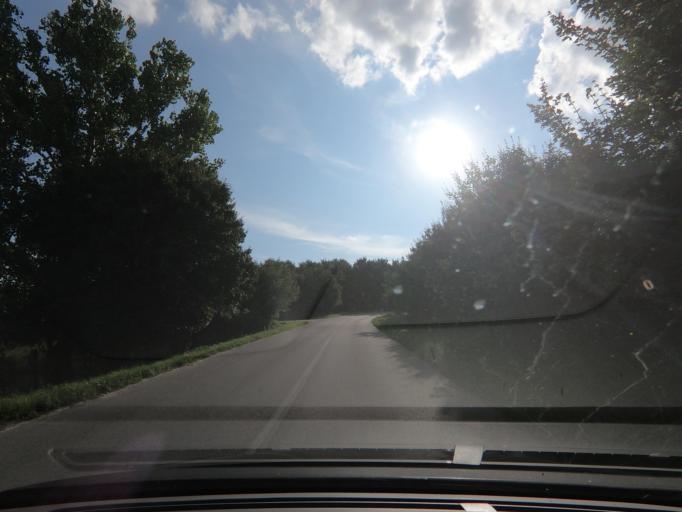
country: SK
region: Nitriansky
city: Stara Tura
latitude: 48.7360
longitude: 17.7163
